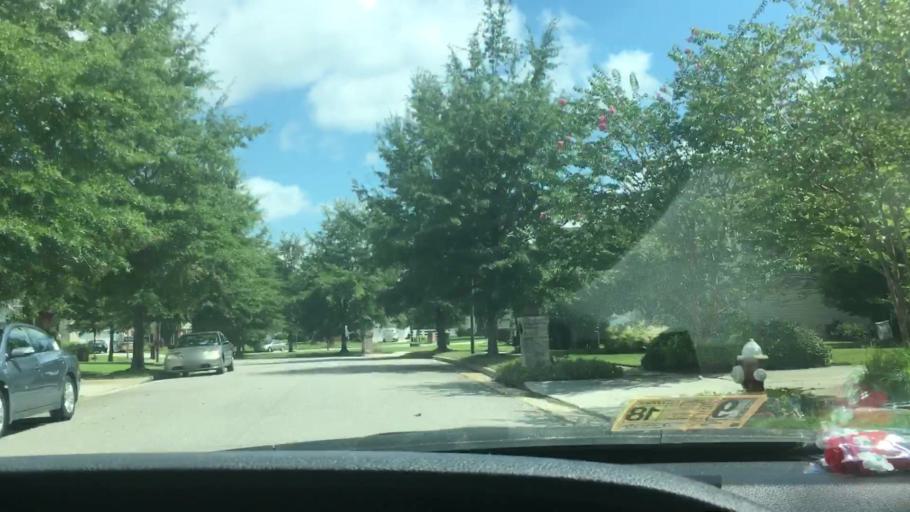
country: US
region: Virginia
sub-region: City of Virginia Beach
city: Virginia Beach
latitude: 36.7264
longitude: -76.0814
